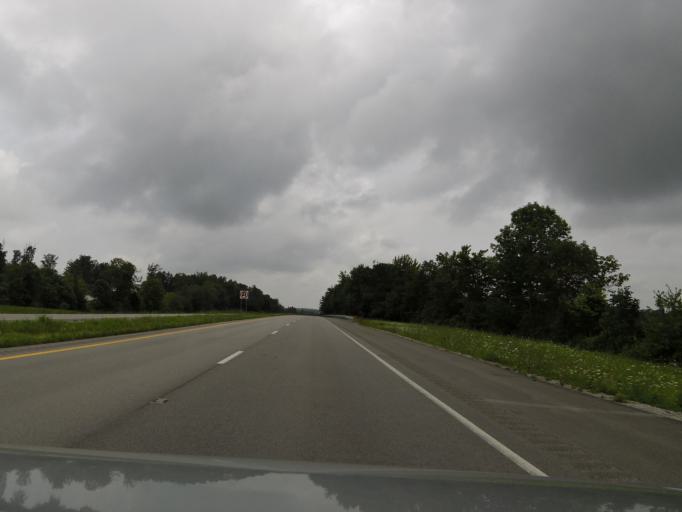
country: US
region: Kentucky
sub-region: Grayson County
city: Leitchfield
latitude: 37.4458
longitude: -86.3474
